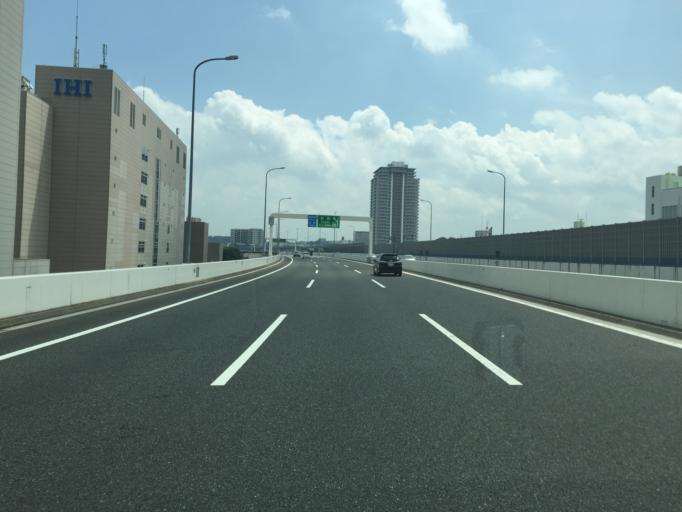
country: JP
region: Kanagawa
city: Yokohama
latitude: 35.3910
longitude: 139.6170
